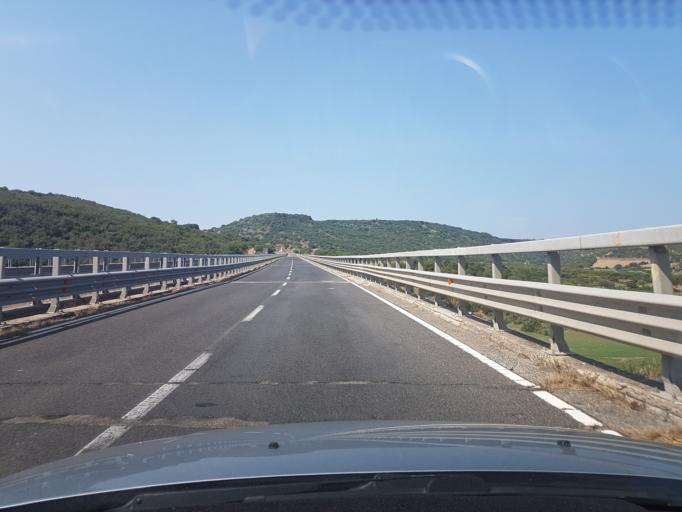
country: IT
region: Sardinia
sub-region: Provincia di Oristano
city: Soddi
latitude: 40.1468
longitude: 8.8801
